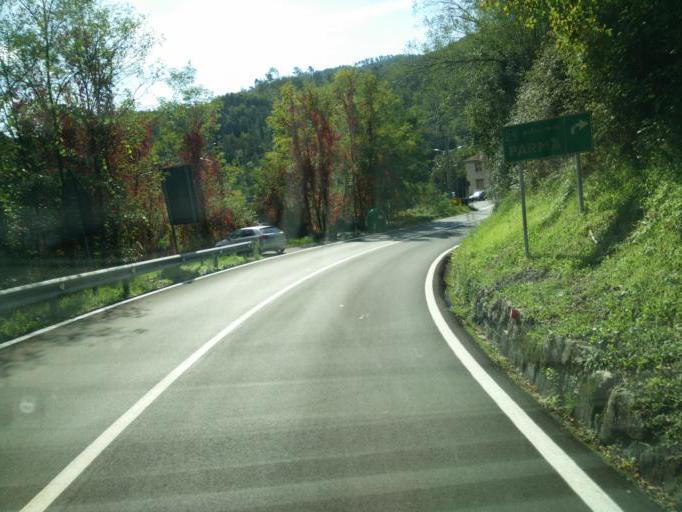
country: IT
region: Liguria
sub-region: Provincia di La Spezia
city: Carrodano
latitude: 44.2411
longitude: 9.6579
